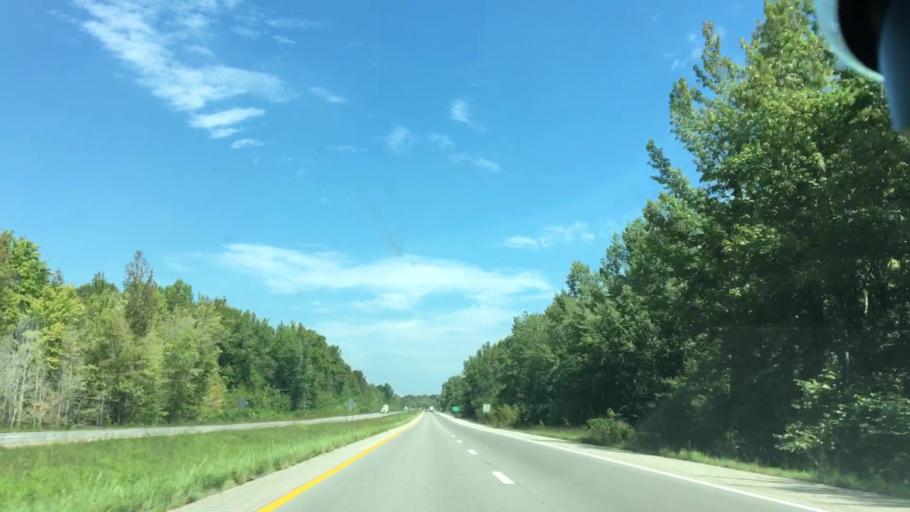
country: US
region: Kentucky
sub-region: Hopkins County
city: Nortonville
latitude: 37.1612
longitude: -87.4575
